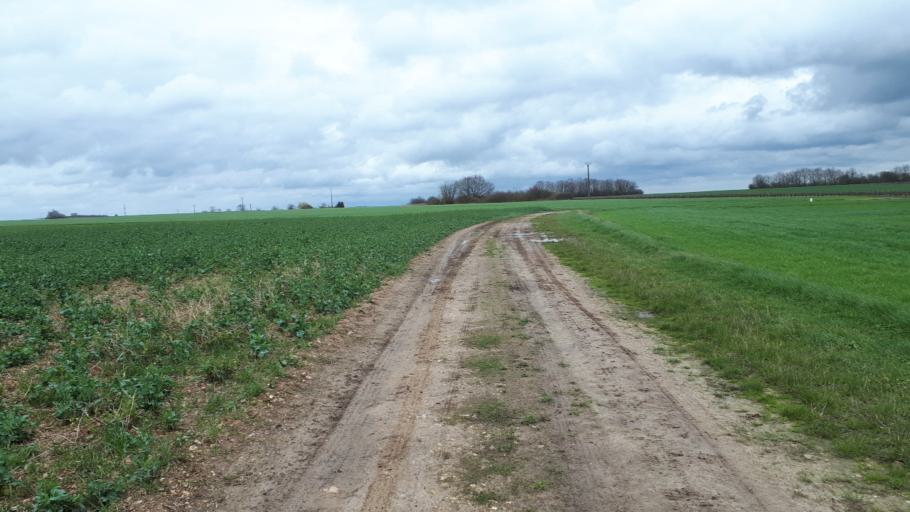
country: FR
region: Centre
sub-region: Departement du Loir-et-Cher
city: Naveil
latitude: 47.8086
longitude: 1.0200
